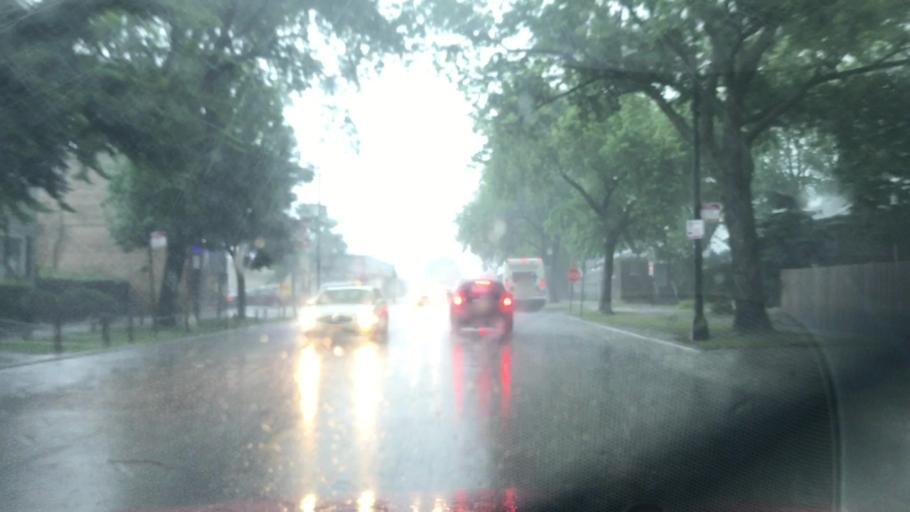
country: US
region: Illinois
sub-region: Cook County
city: Oak Park
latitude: 41.8779
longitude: -87.7549
